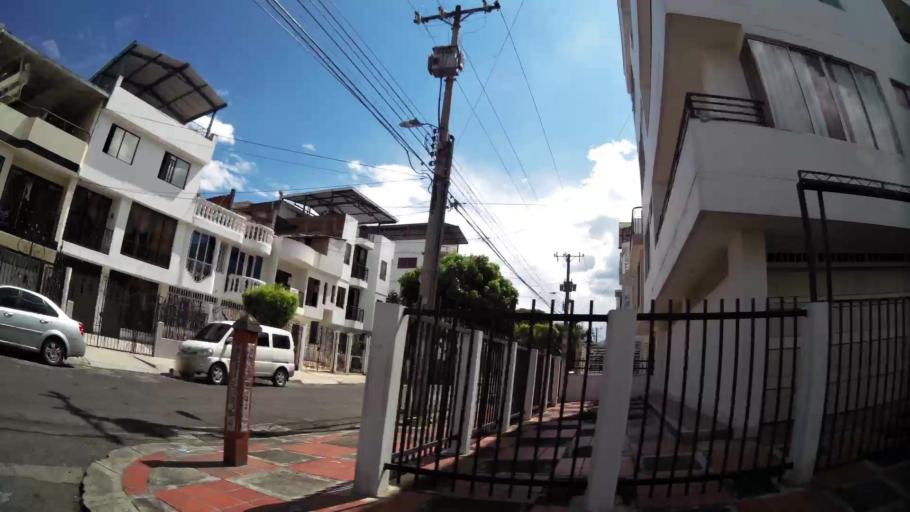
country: CO
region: Valle del Cauca
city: Cali
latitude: 3.3976
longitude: -76.5182
